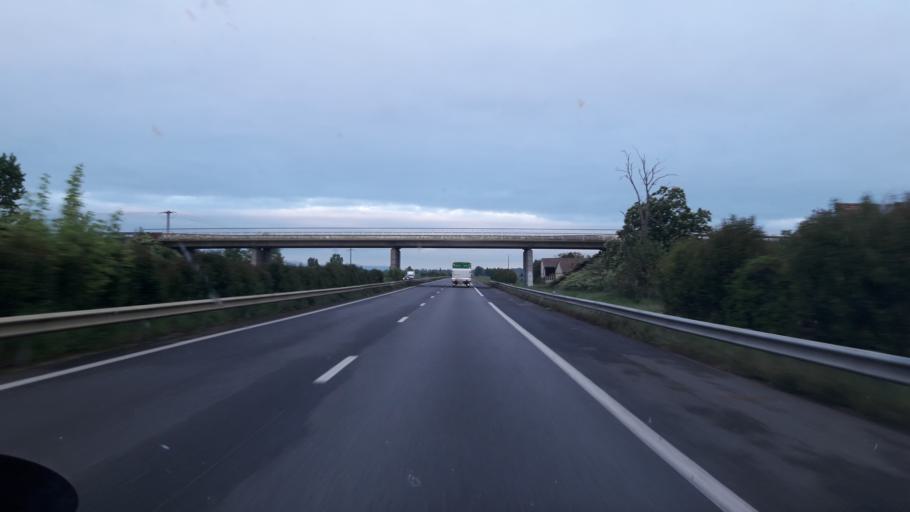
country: FR
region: Midi-Pyrenees
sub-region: Departement de la Haute-Garonne
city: Rieux-Volvestre
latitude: 43.2918
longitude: 1.1692
